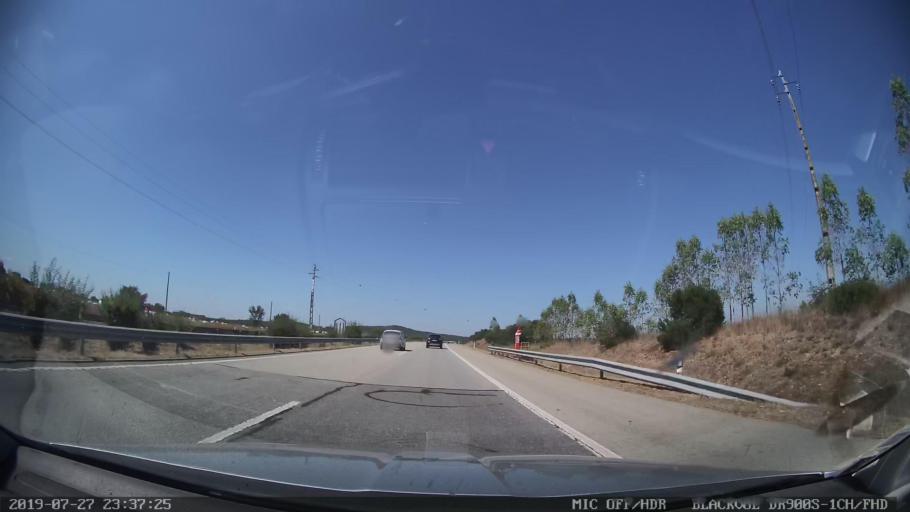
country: PT
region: Evora
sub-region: Montemor-O-Novo
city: Montemor-o-Novo
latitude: 38.6460
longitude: -8.2576
